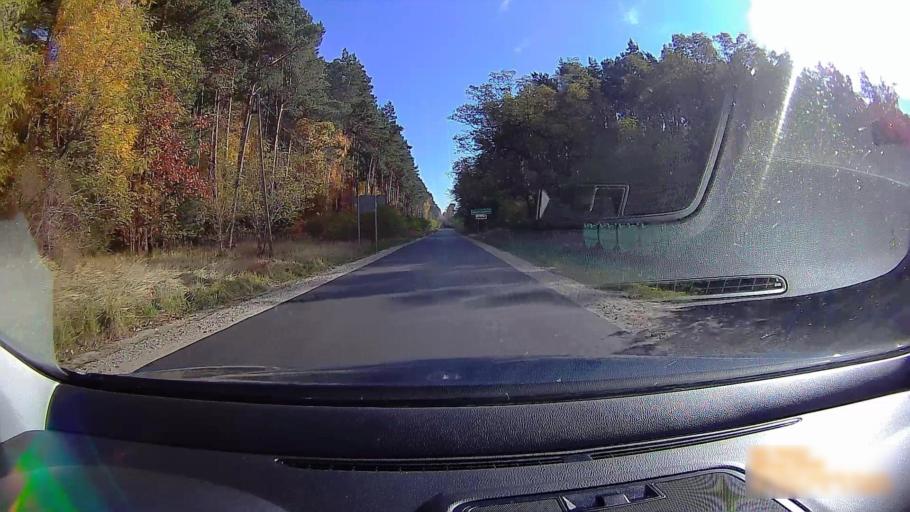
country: PL
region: Greater Poland Voivodeship
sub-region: Powiat ostrzeszowski
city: Ostrzeszow
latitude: 51.4105
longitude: 17.9935
